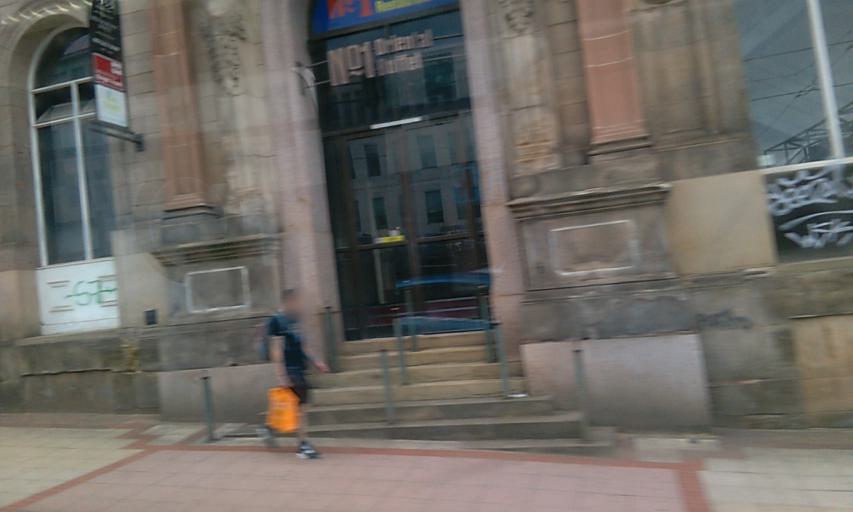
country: GB
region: England
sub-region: Sheffield
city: Sheffield
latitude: 53.3831
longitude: -1.4632
